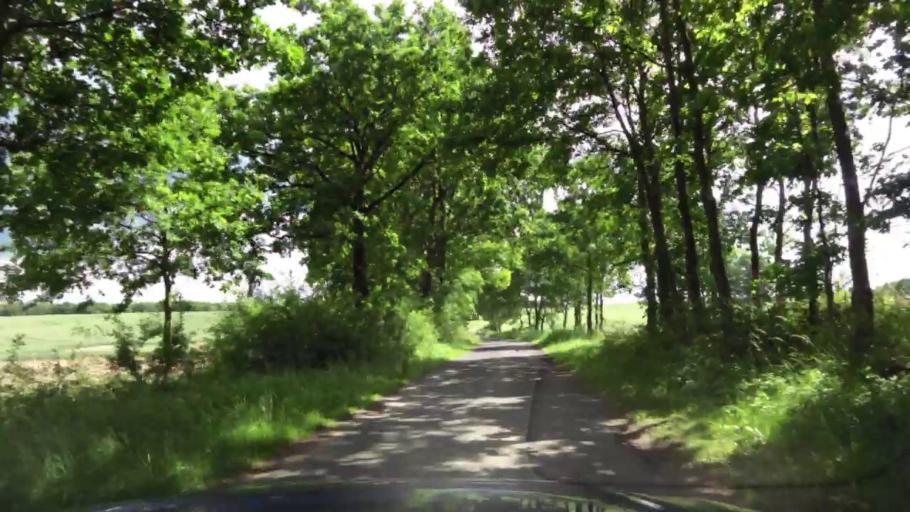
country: PL
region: West Pomeranian Voivodeship
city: Trzcinsko Zdroj
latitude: 52.9051
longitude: 14.6047
